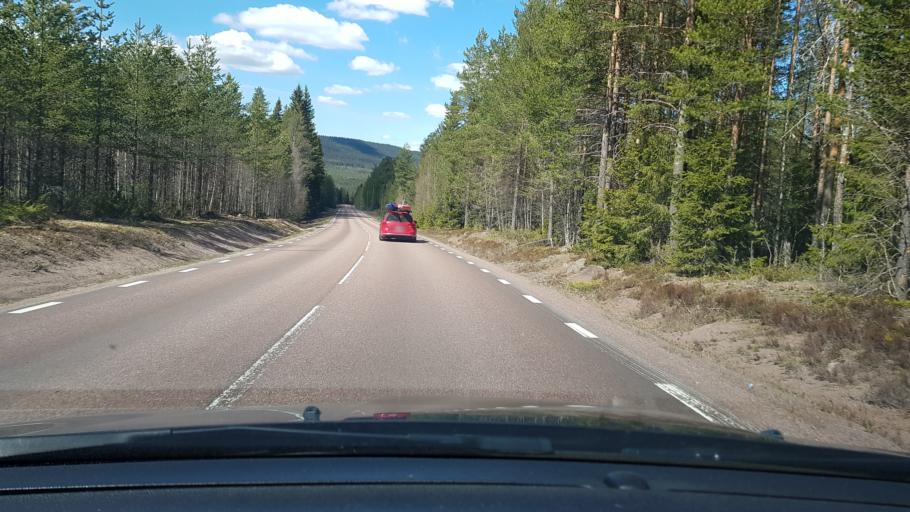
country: SE
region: Dalarna
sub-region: Malung-Saelens kommun
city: Malung
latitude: 61.0588
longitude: 13.3550
